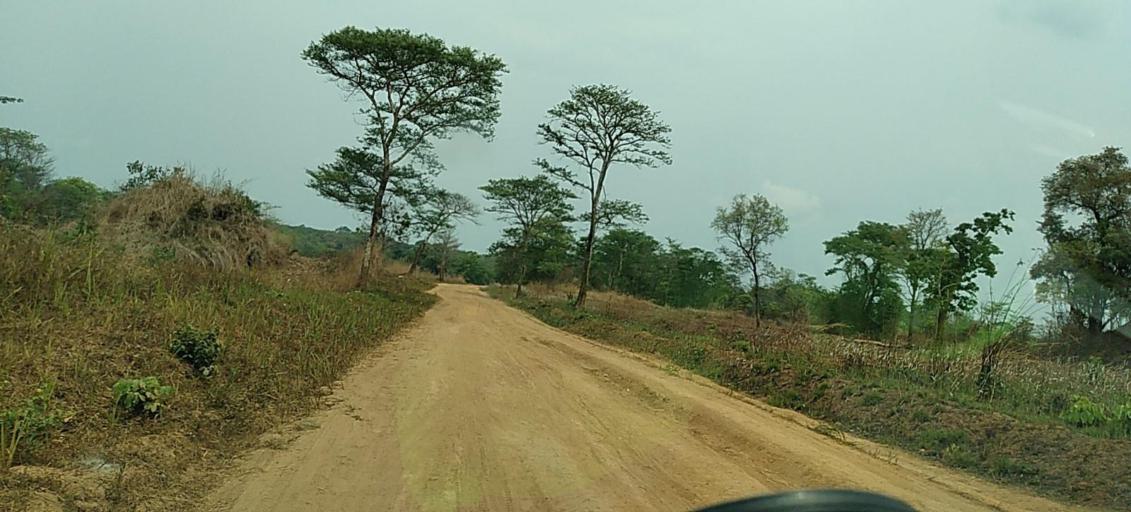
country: ZM
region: North-Western
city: Solwezi
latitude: -12.7933
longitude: 26.5315
